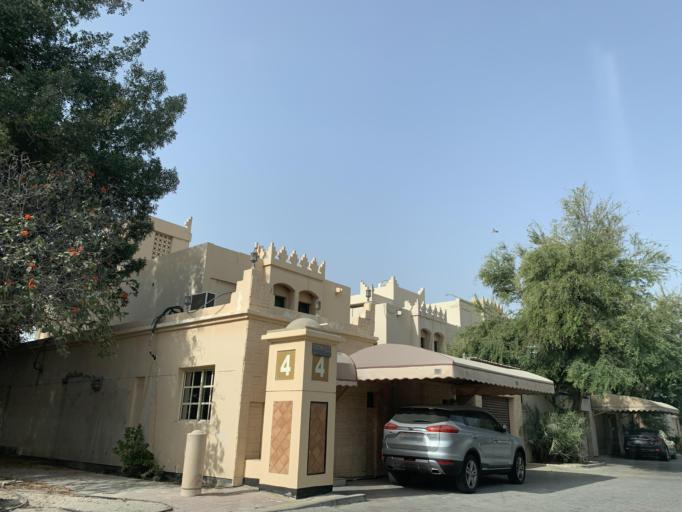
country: BH
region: Northern
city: Madinat `Isa
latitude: 26.1692
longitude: 50.5371
